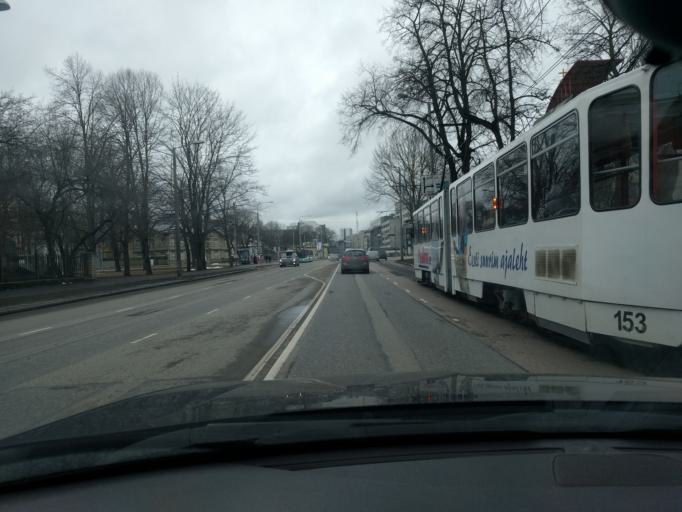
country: EE
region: Harju
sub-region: Tallinna linn
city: Tallinn
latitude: 59.4396
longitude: 24.7780
